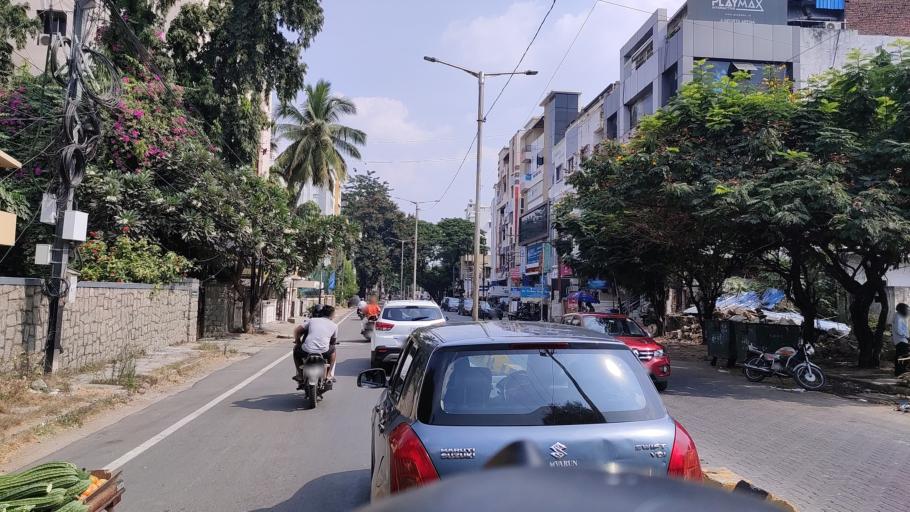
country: IN
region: Telangana
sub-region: Hyderabad
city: Hyderabad
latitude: 17.4301
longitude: 78.4440
